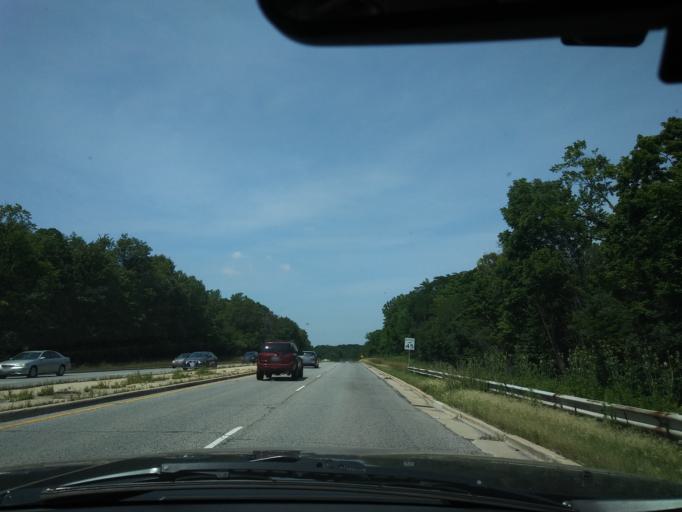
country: US
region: Illinois
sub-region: Cook County
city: Tinley Park
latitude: 41.6179
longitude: -87.7946
